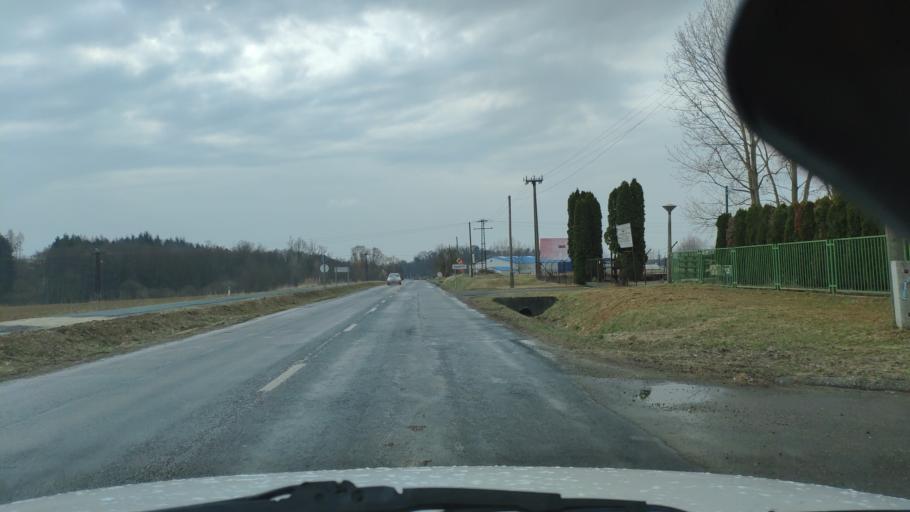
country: HU
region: Zala
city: Nagykanizsa
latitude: 46.4223
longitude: 16.9857
